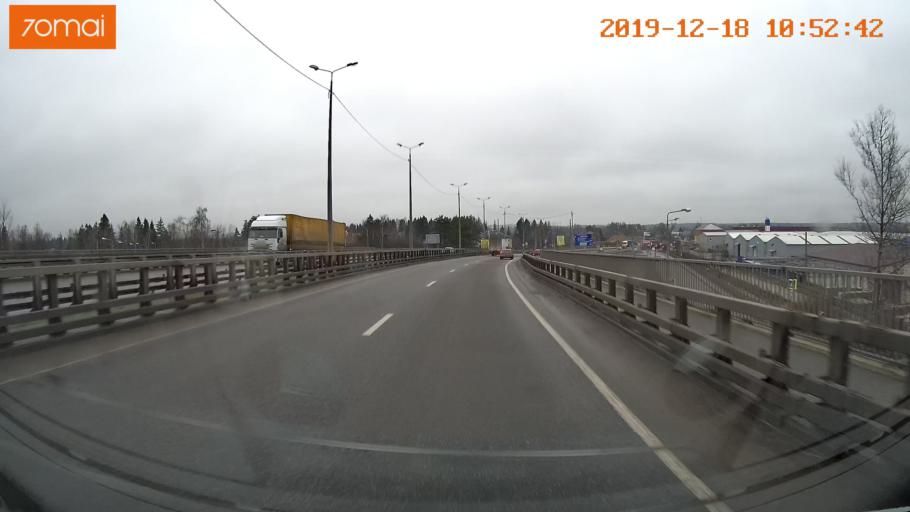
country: RU
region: Moskovskaya
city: Selyatino
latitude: 55.5272
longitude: 36.9780
